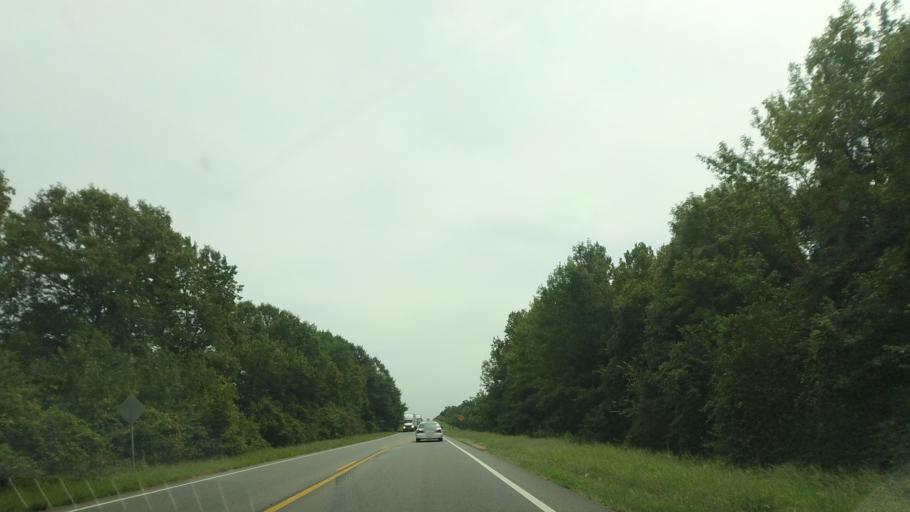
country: US
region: Georgia
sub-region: Houston County
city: Robins Air Force Base
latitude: 32.5428
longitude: -83.5408
